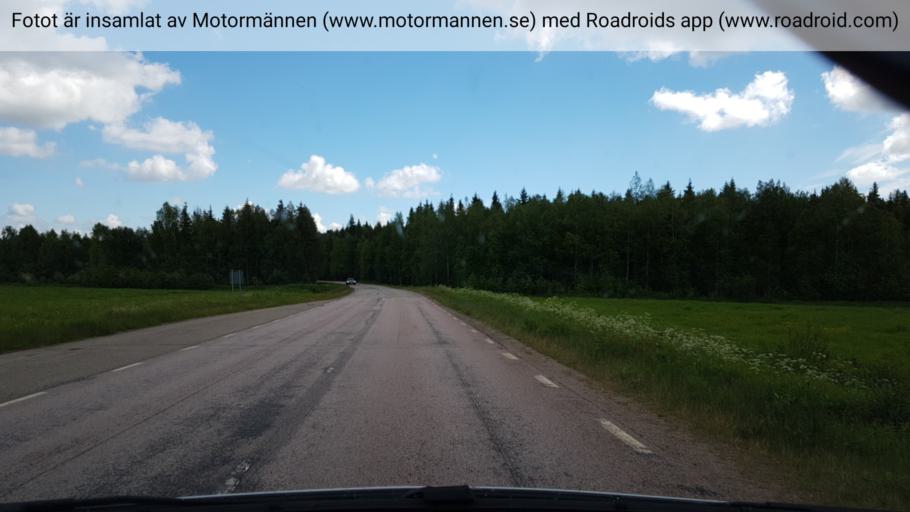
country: FI
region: Lapland
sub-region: Torniolaakso
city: Ylitornio
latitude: 66.1848
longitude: 23.7260
